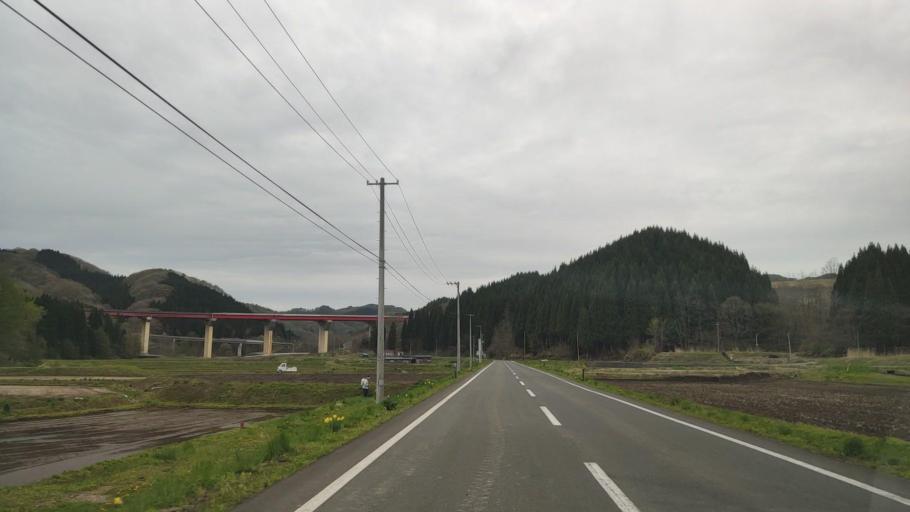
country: JP
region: Akita
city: Odate
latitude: 40.3716
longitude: 140.7225
